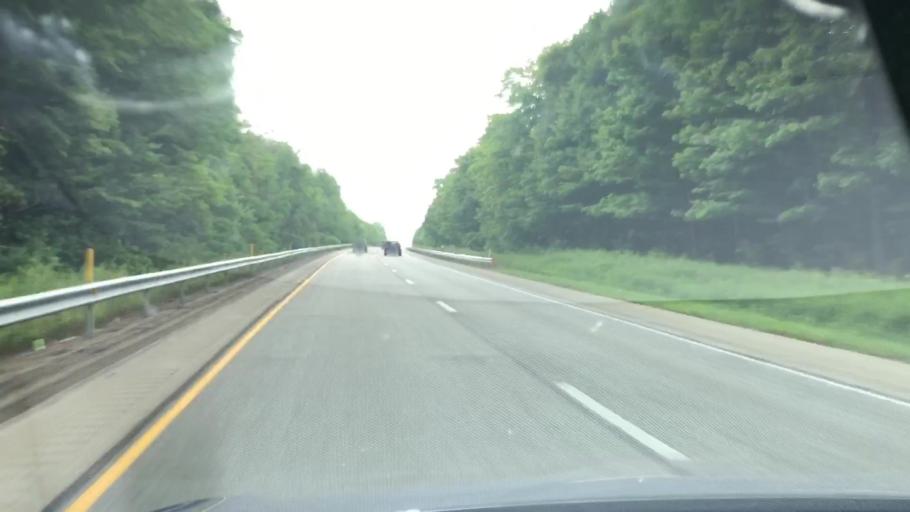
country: US
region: Pennsylvania
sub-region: Erie County
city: Edinboro
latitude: 41.9205
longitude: -80.1761
